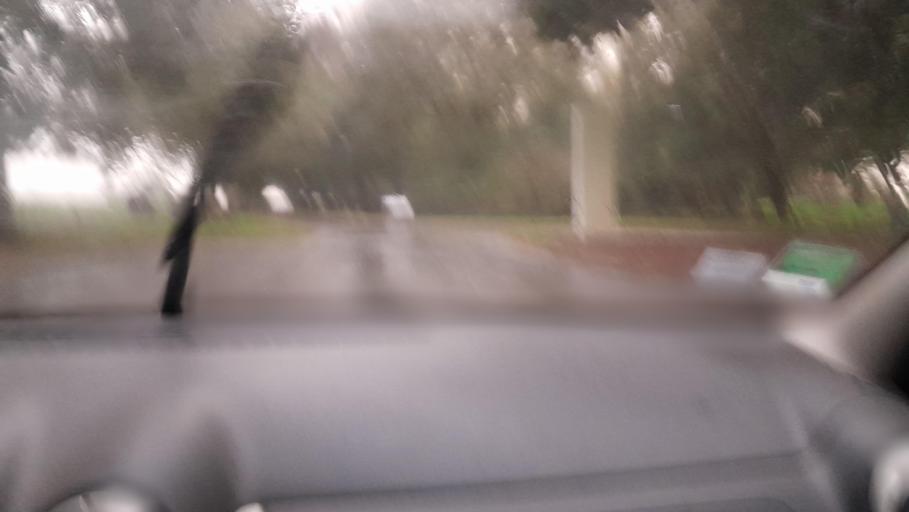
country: FR
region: Pays de la Loire
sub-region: Departement de la Mayenne
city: Ballots
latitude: 47.8633
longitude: -1.0681
